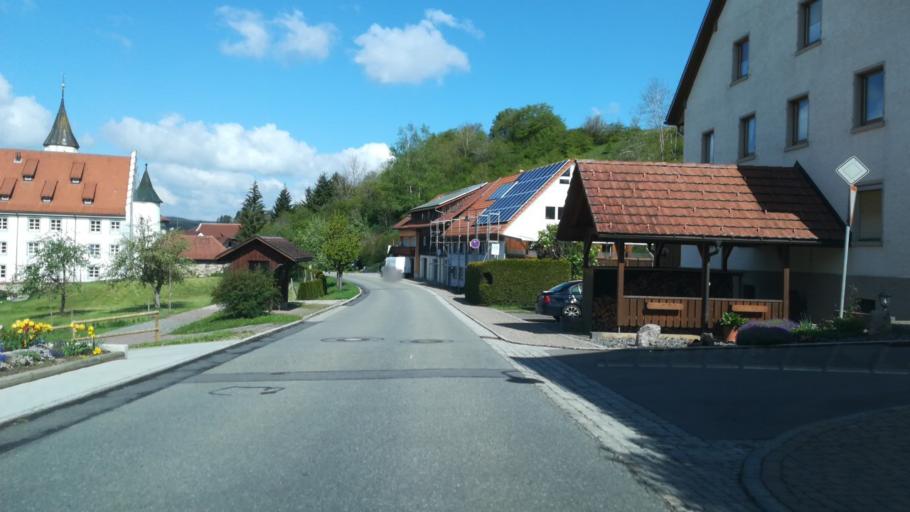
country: DE
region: Baden-Wuerttemberg
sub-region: Freiburg Region
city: Uhlingen-Birkendorf
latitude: 47.7525
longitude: 8.3672
